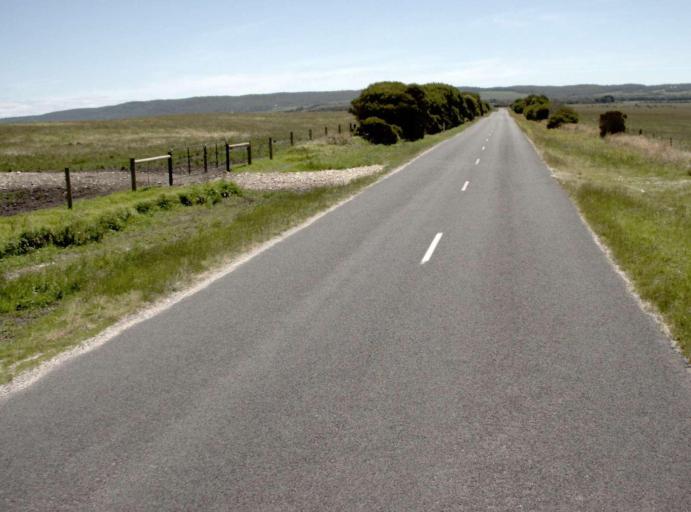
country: AU
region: Victoria
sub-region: Bass Coast
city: North Wonthaggi
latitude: -38.8108
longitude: 146.0952
